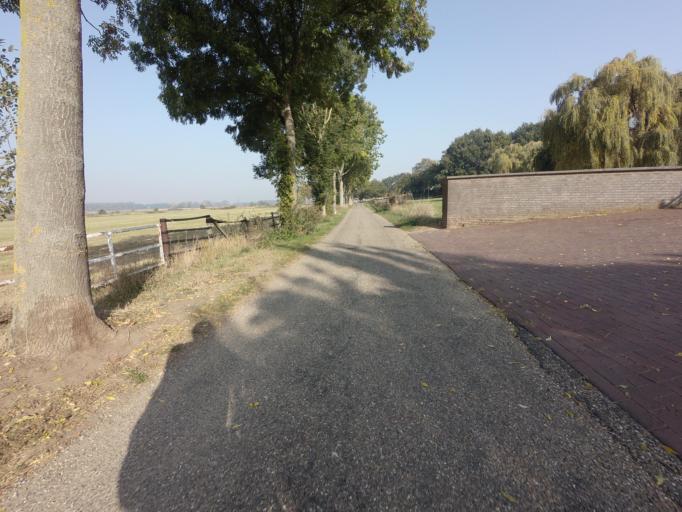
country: NL
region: Limburg
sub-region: Gemeente Roermond
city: Leeuwen
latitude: 51.2121
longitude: 5.9926
